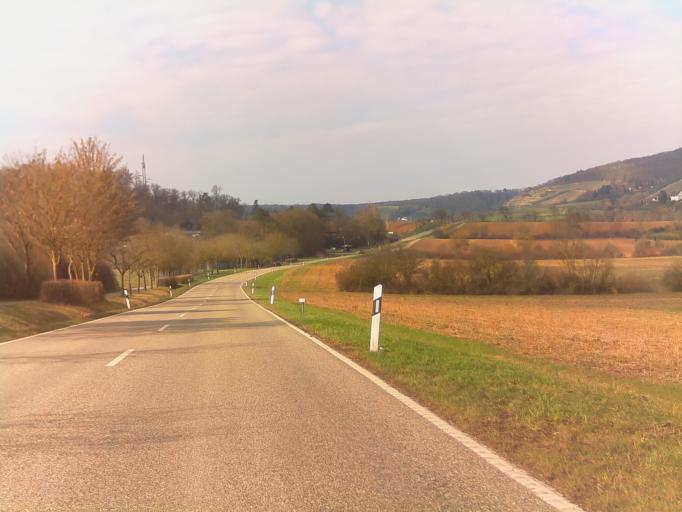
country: DE
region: Baden-Wuerttemberg
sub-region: Regierungsbezirk Stuttgart
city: Sersheim
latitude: 49.0060
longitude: 9.0066
